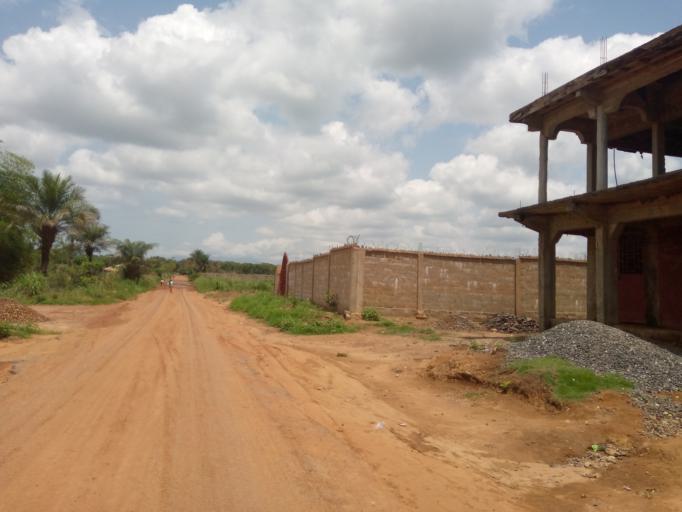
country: SL
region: Western Area
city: Waterloo
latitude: 8.3855
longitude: -12.9546
